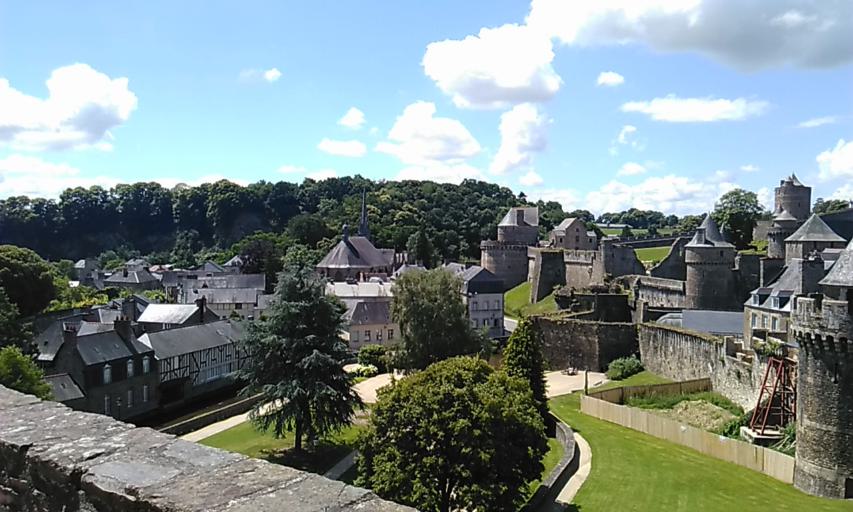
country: FR
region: Brittany
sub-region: Departement d'Ille-et-Vilaine
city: Fougeres
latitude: 48.3545
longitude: -1.2064
